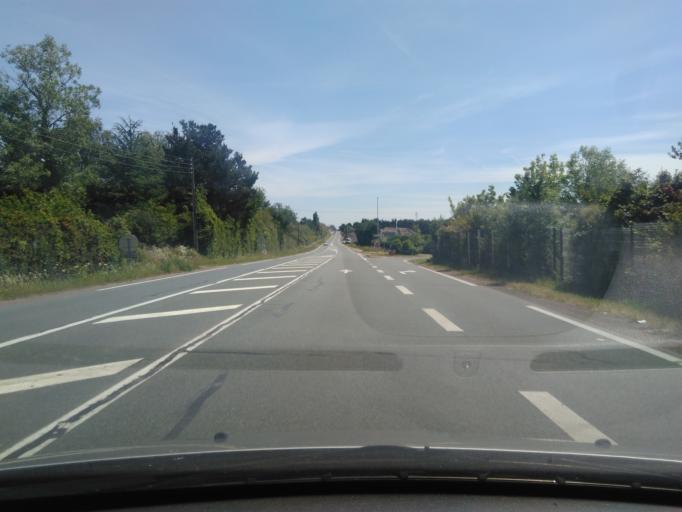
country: FR
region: Pays de la Loire
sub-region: Departement de la Vendee
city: La Roche-sur-Yon
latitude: 46.6444
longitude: -1.4112
